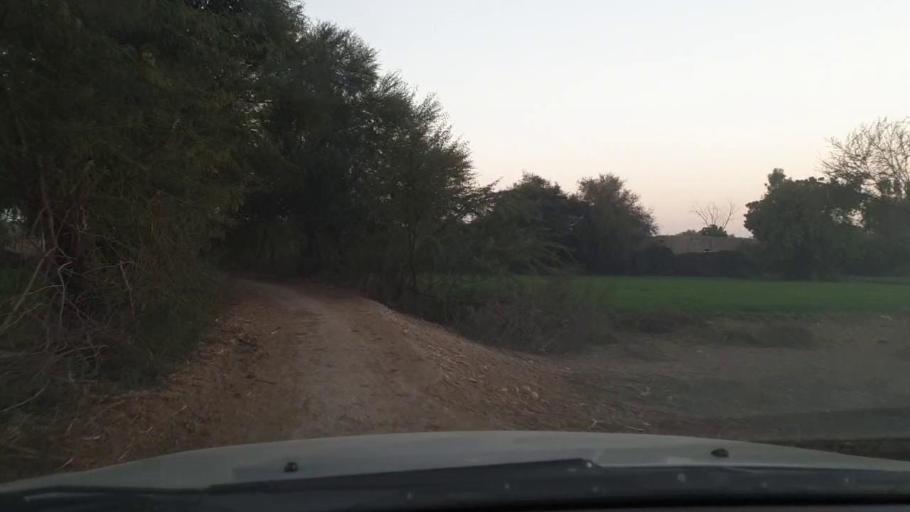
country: PK
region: Sindh
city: Mirpur Mathelo
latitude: 28.0214
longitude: 69.5193
